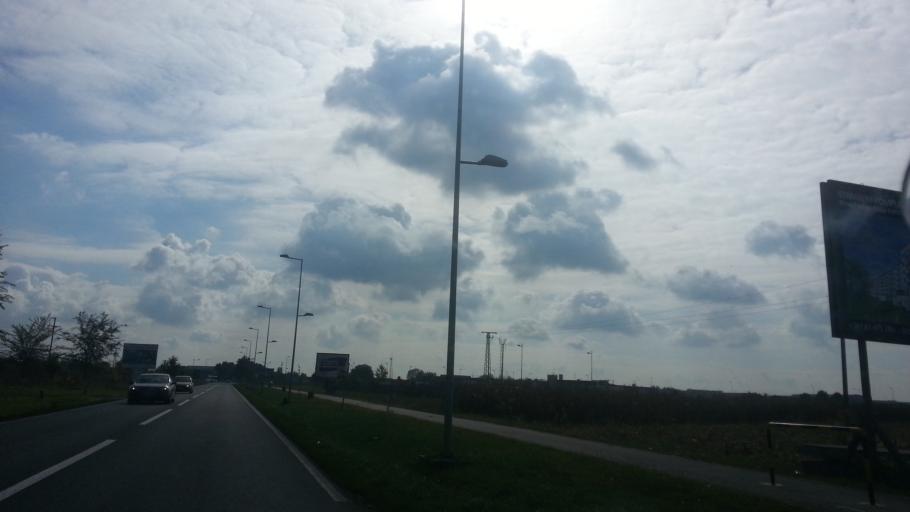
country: RS
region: Autonomna Pokrajina Vojvodina
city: Nova Pazova
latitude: 44.9591
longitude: 20.1968
